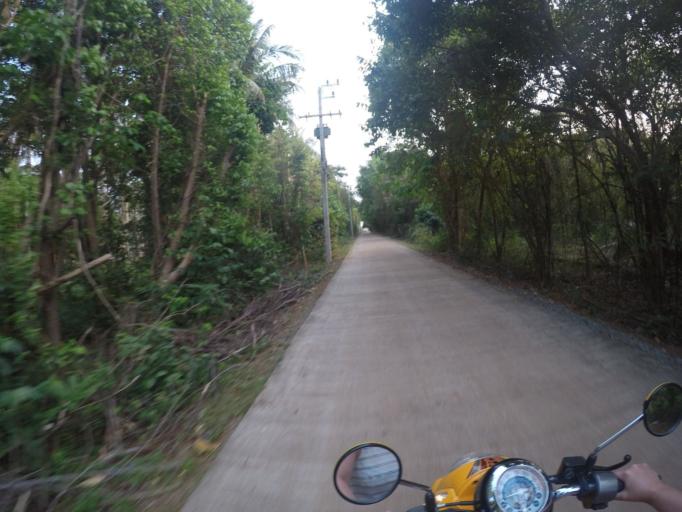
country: TH
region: Trat
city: Ko Kut
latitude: 11.7966
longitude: 102.4873
